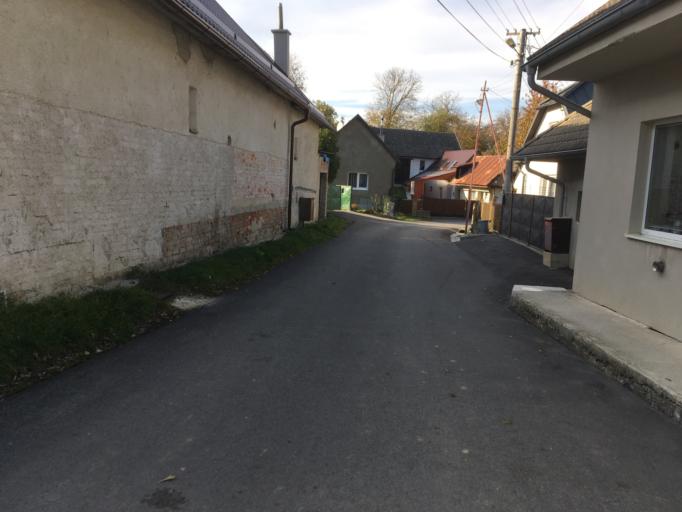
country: SK
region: Trenciansky
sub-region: Okres Povazska Bystrica
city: Povazska Bystrica
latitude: 49.0511
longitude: 18.4073
